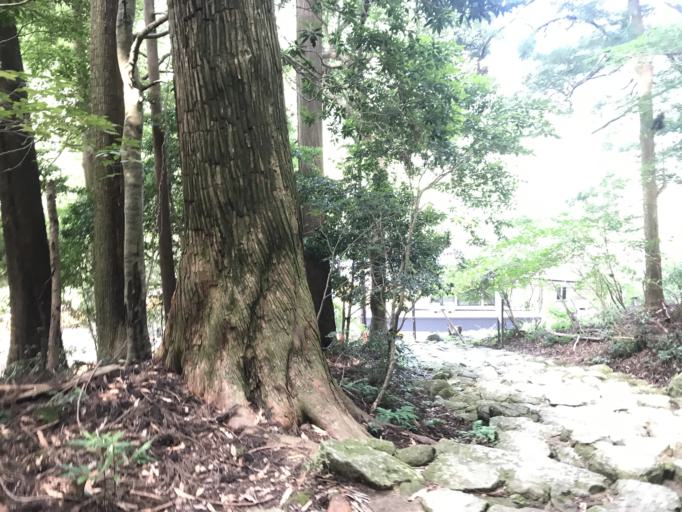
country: JP
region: Wakayama
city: Shingu
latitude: 33.6724
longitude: 135.8896
